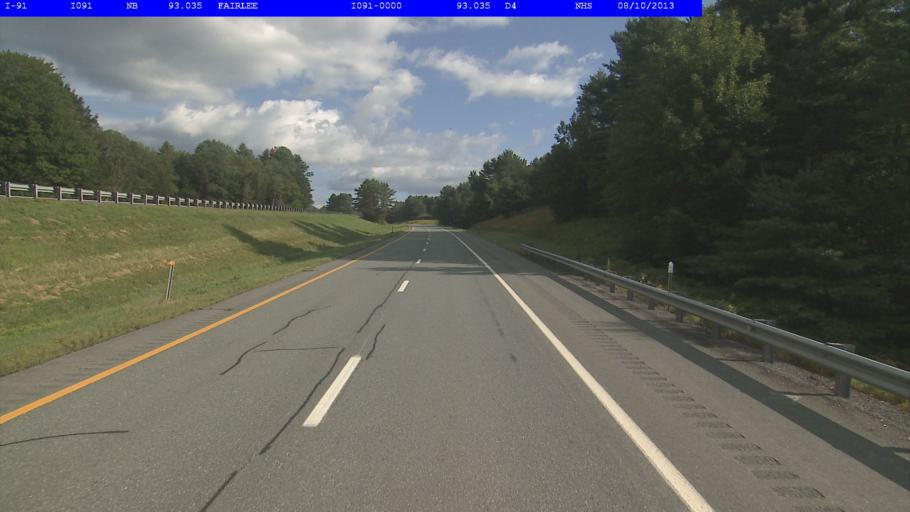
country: US
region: New Hampshire
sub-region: Grafton County
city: Orford
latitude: 43.9191
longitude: -72.1328
